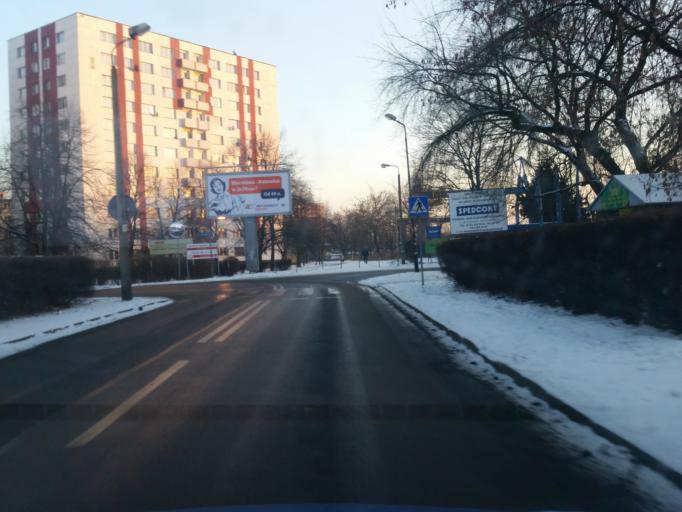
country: PL
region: Silesian Voivodeship
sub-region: Sosnowiec
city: Sosnowiec
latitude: 50.2700
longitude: 19.1266
